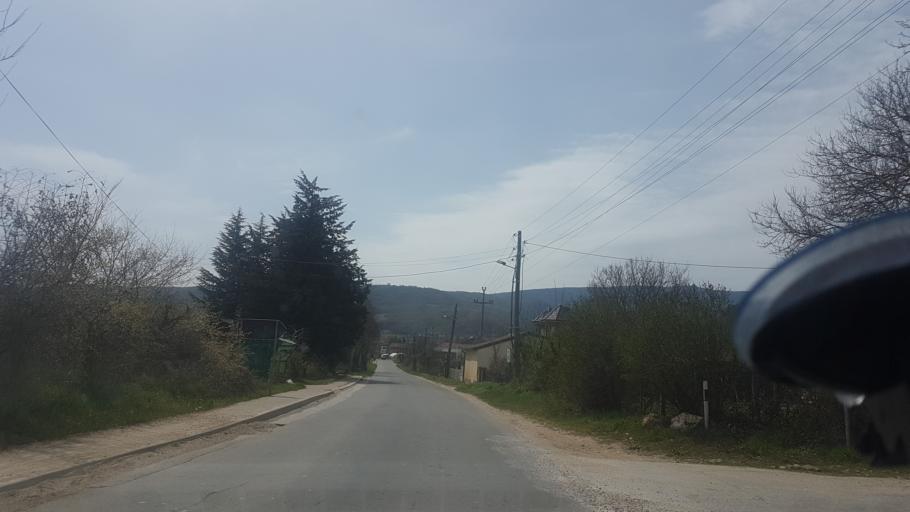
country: MK
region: Zelenikovo
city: Zelenikovo
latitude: 41.8896
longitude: 21.5877
